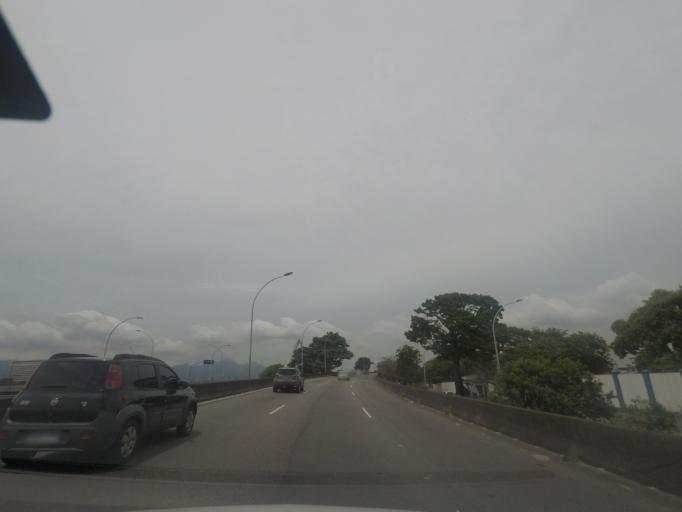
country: BR
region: Rio de Janeiro
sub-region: Rio De Janeiro
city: Rio de Janeiro
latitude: -22.8320
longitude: -43.2376
